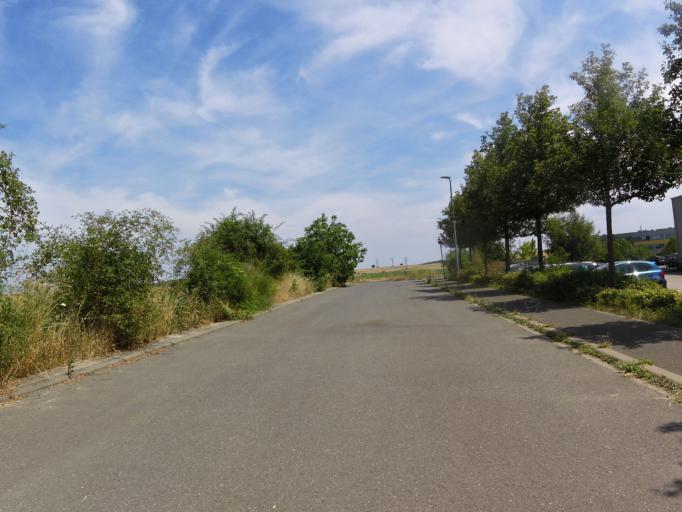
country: DE
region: Bavaria
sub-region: Regierungsbezirk Unterfranken
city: Estenfeld
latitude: 49.8042
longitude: 10.0001
